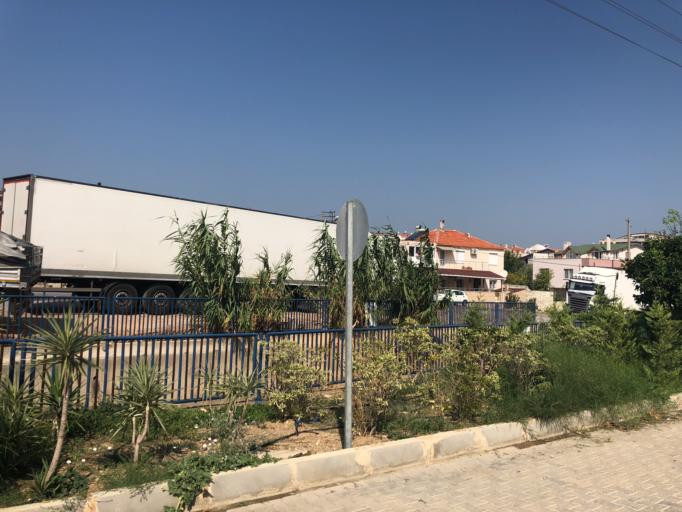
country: TR
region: Izmir
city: Urla
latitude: 38.3259
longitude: 26.7644
